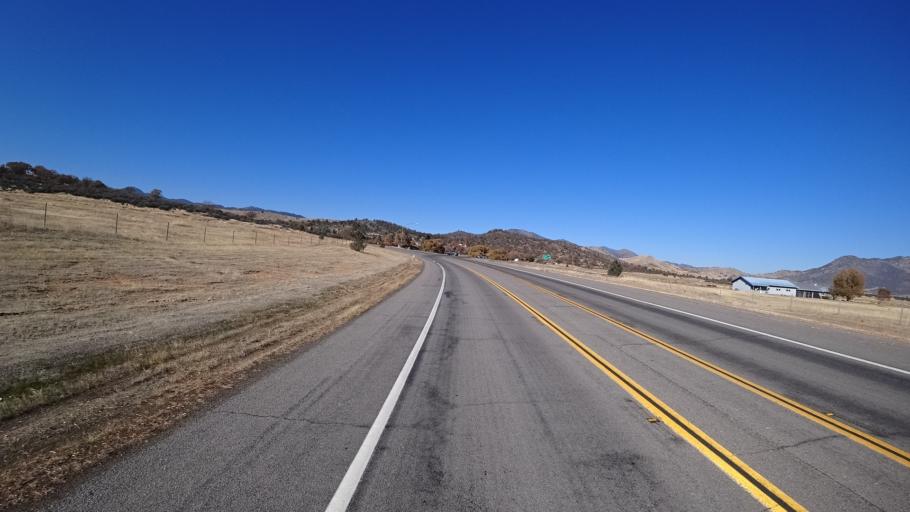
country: US
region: California
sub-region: Siskiyou County
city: Yreka
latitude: 41.7401
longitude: -122.5979
